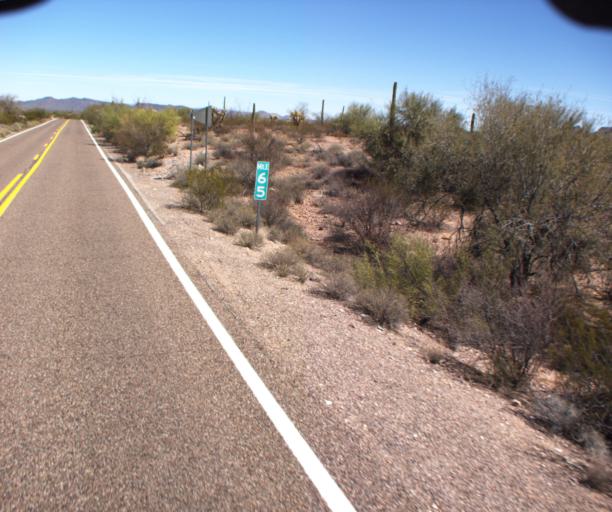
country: MX
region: Sonora
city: Sonoyta
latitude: 32.0960
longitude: -112.7729
